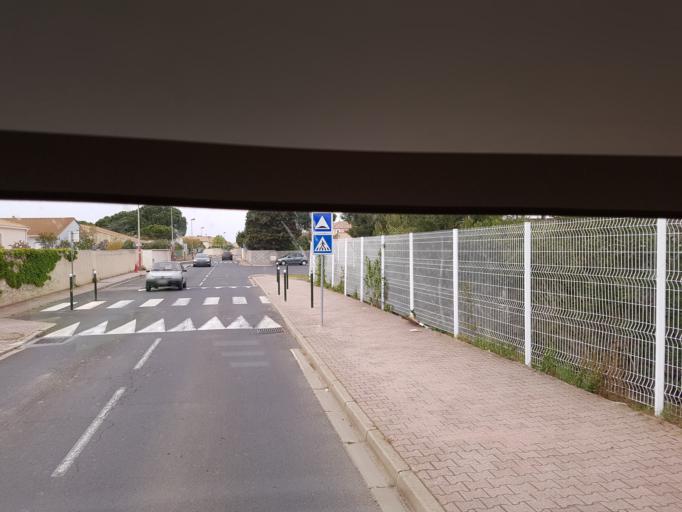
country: FR
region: Languedoc-Roussillon
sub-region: Departement de l'Herault
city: Serignan
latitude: 43.2766
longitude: 3.2708
